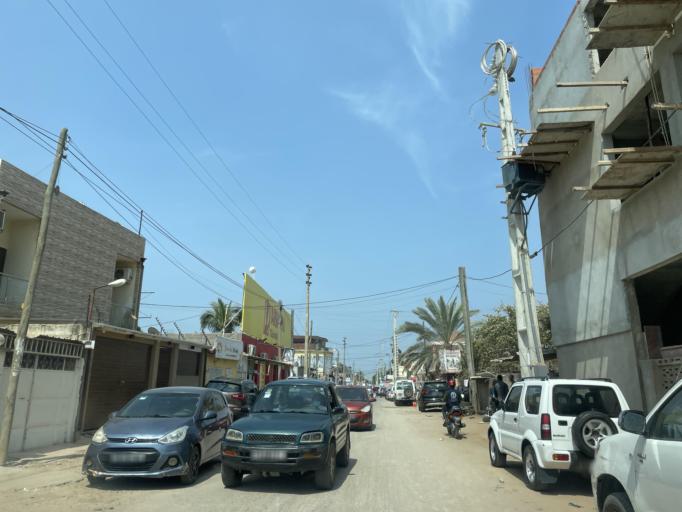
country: AO
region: Luanda
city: Luanda
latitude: -8.8992
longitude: 13.1855
